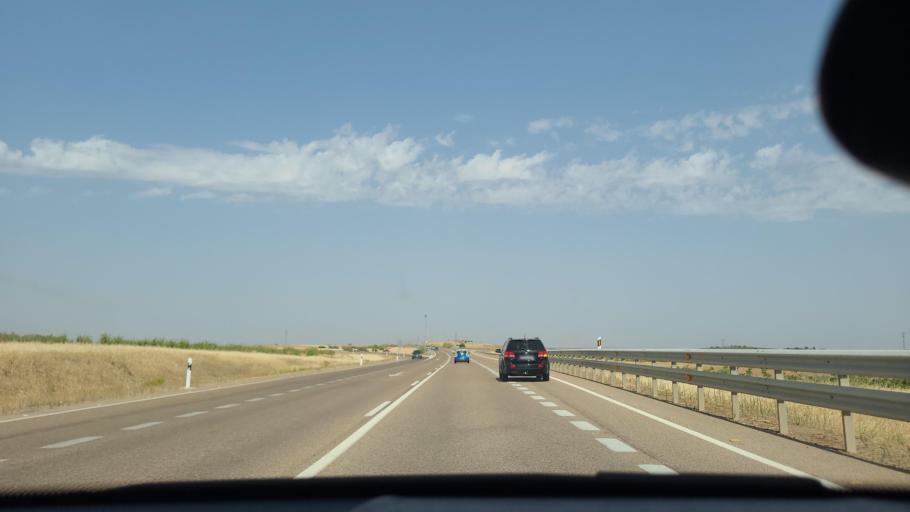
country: ES
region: Extremadura
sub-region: Provincia de Badajoz
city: Santa Marta
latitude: 38.5886
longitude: -6.6038
